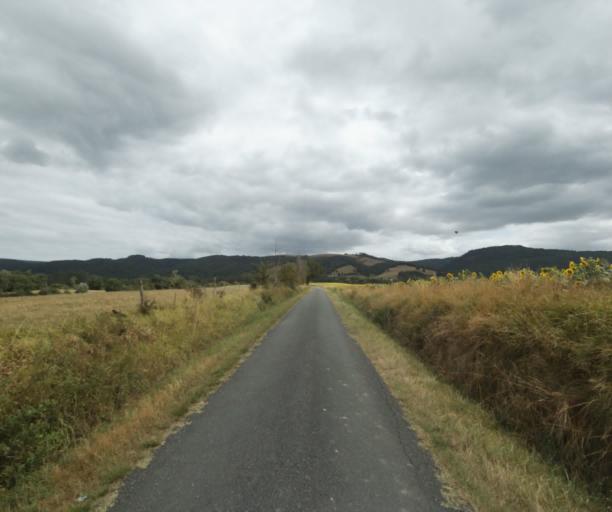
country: FR
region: Midi-Pyrenees
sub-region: Departement du Tarn
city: Soreze
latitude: 43.4644
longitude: 2.0699
